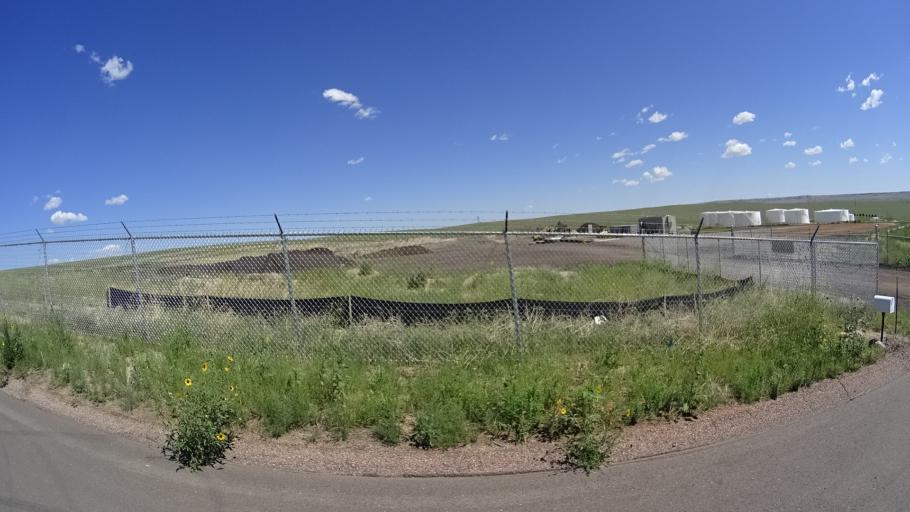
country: US
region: Colorado
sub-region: El Paso County
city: Security-Widefield
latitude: 38.7810
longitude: -104.6809
